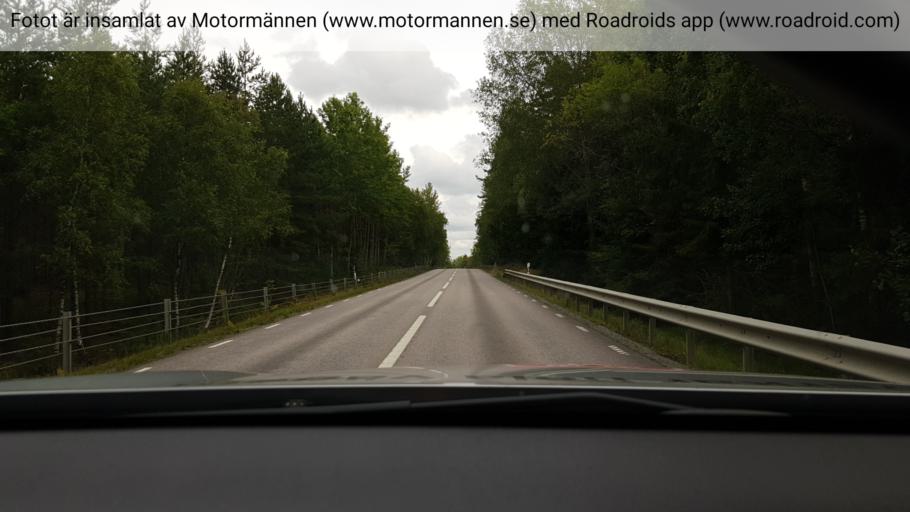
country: SE
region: Stockholm
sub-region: Sigtuna Kommun
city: Sigtuna
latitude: 59.6510
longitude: 17.6533
